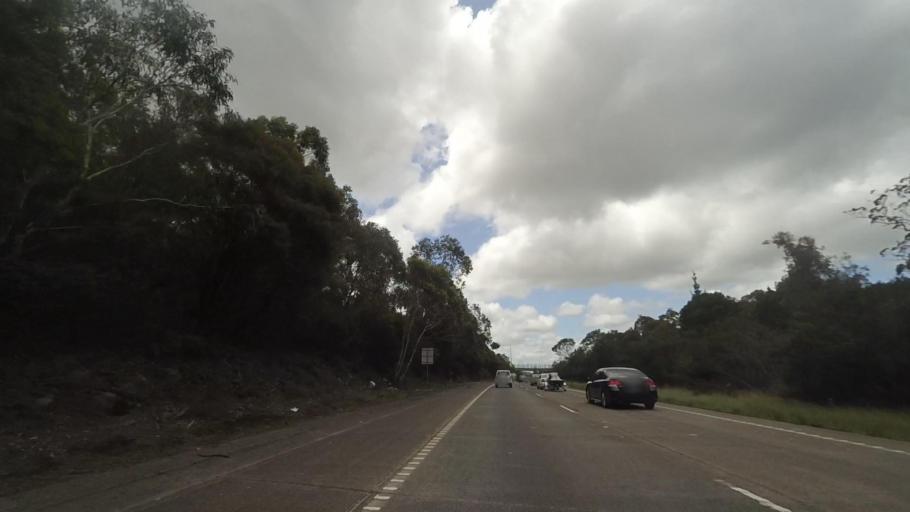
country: AU
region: New South Wales
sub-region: Gosford Shire
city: Narara
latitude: -33.3981
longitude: 151.2969
